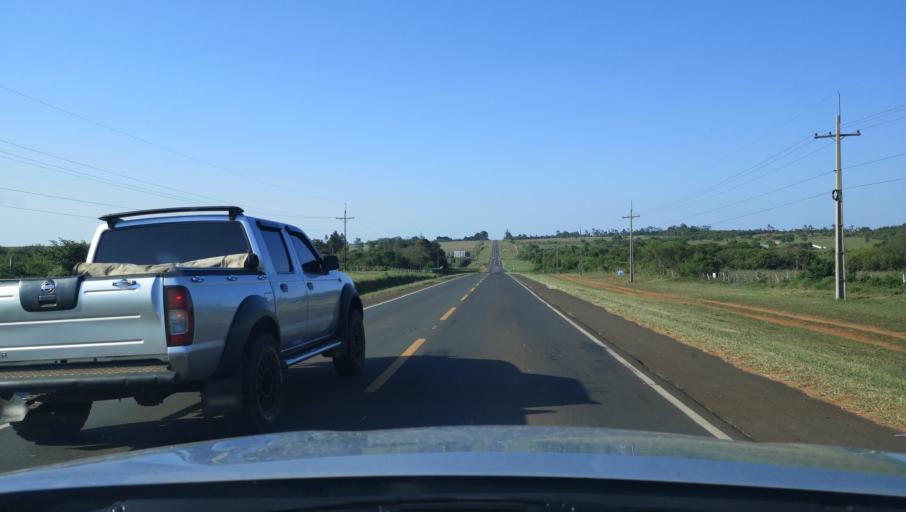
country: PY
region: Misiones
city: Santa Maria
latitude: -26.8363
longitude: -57.0339
